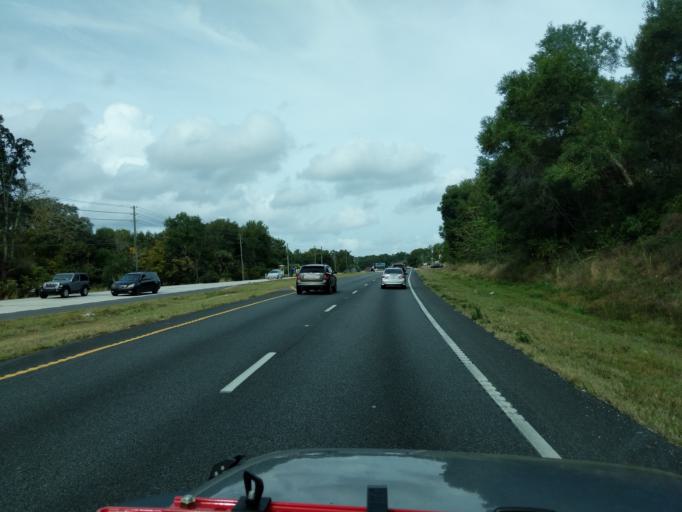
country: US
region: Florida
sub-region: Orange County
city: Zellwood
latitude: 28.7399
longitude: -81.6157
